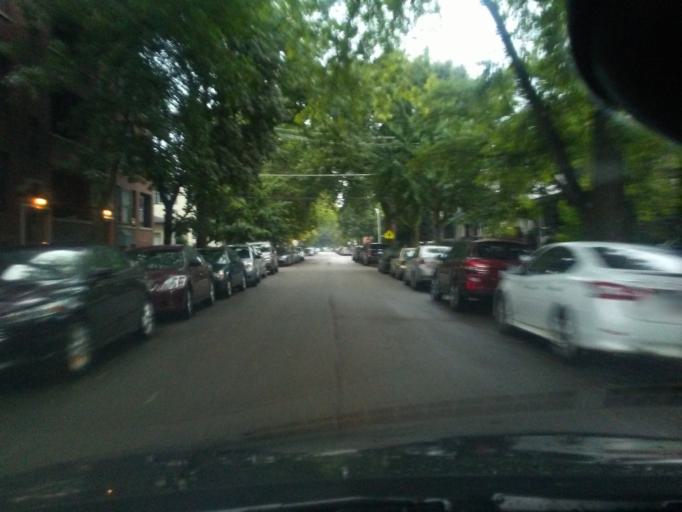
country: US
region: Illinois
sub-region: Cook County
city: Evanston
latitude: 41.9963
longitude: -87.6678
